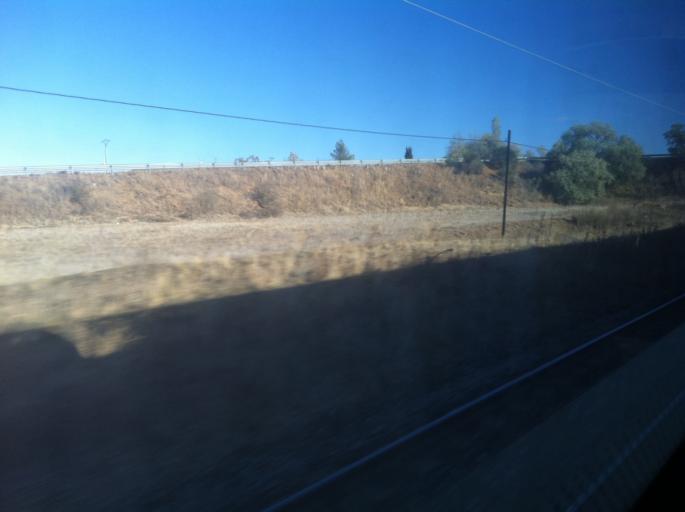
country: ES
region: Castille and Leon
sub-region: Provincia de Burgos
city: Villazopeque
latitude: 42.1868
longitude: -4.0370
